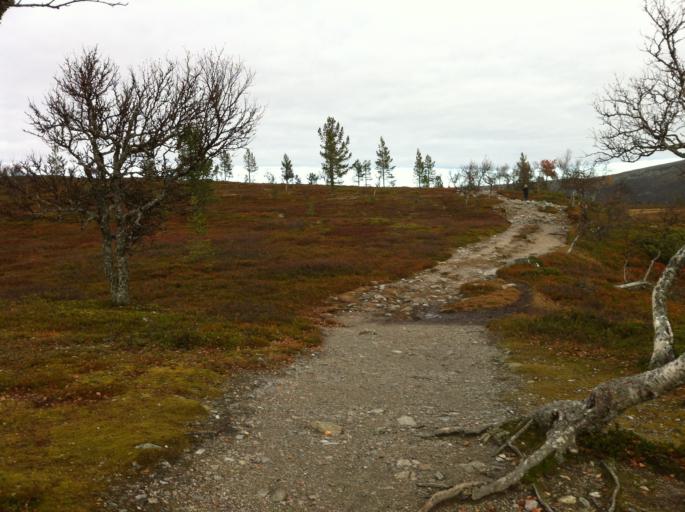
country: NO
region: Hedmark
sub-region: Engerdal
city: Engerdal
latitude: 62.0972
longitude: 12.2655
